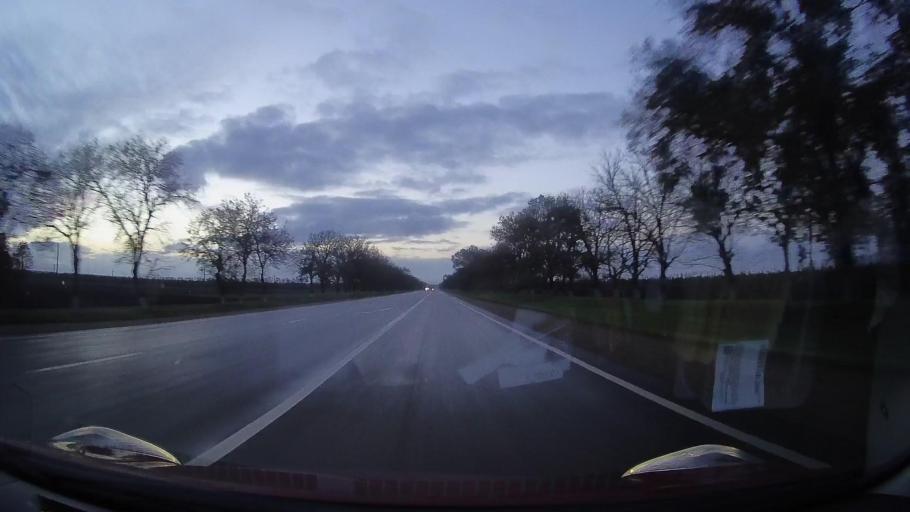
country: RU
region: Krasnodarskiy
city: Zavetnyy
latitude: 44.8990
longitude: 41.1888
